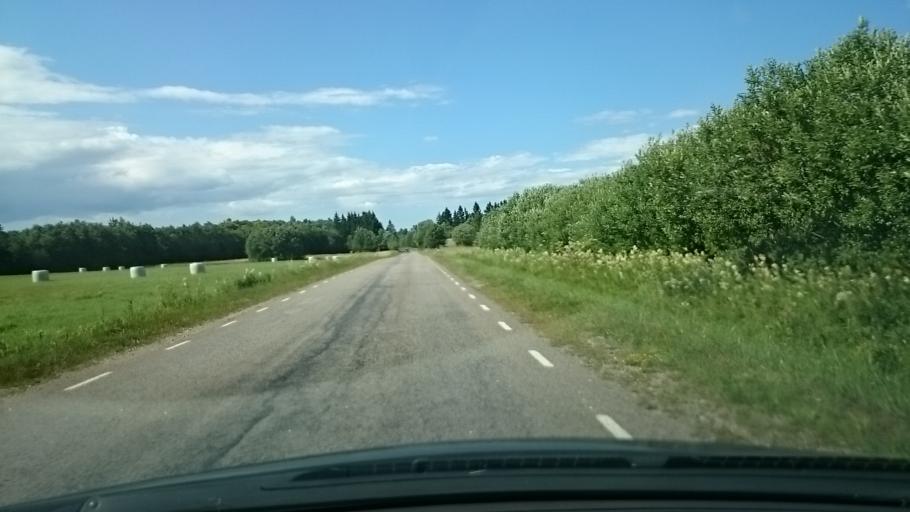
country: EE
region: Laeaene
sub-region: Haapsalu linn
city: Haapsalu
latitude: 59.0799
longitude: 23.5599
